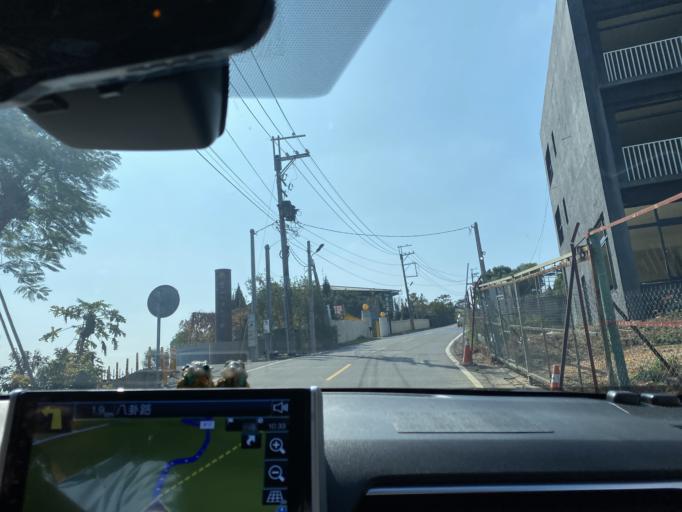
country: TW
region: Taiwan
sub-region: Nantou
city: Nantou
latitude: 23.9430
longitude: 120.6515
